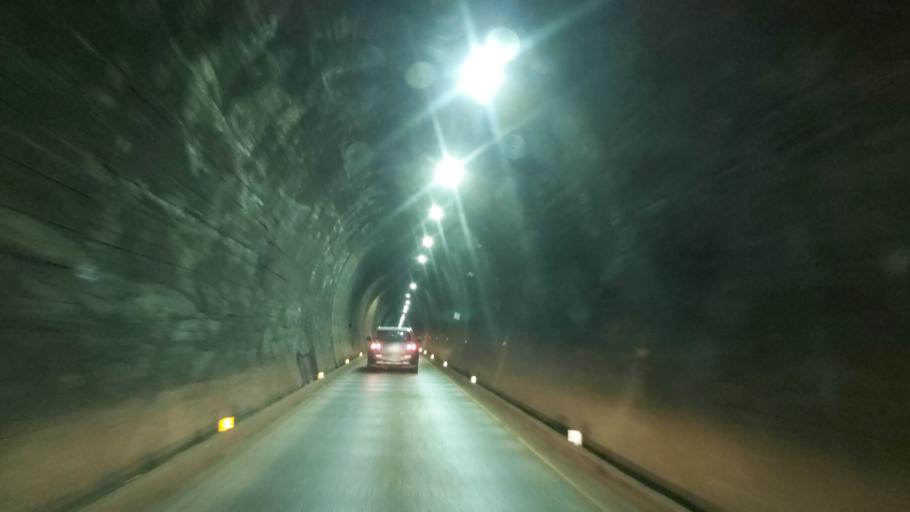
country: CL
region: Araucania
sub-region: Provincia de Cautin
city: Vilcun
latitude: -38.5199
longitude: -71.5155
